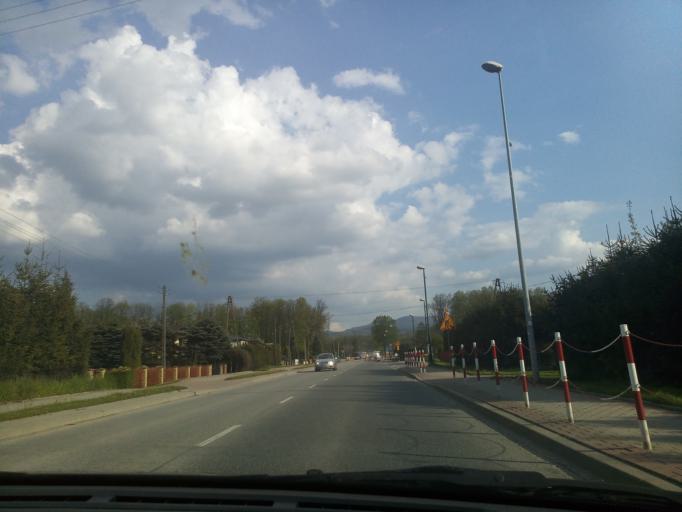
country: PL
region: Lesser Poland Voivodeship
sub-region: Powiat nowosadecki
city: Nawojowa
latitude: 49.5681
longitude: 20.7385
